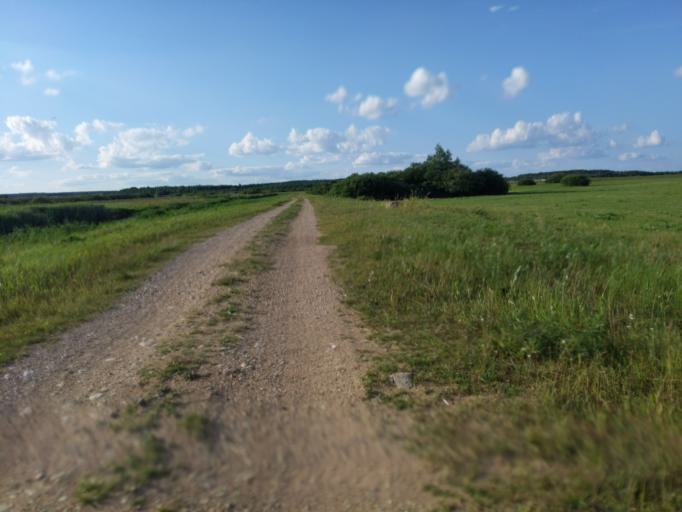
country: BY
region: Minsk
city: Nyasvizh
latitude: 53.2373
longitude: 26.7093
